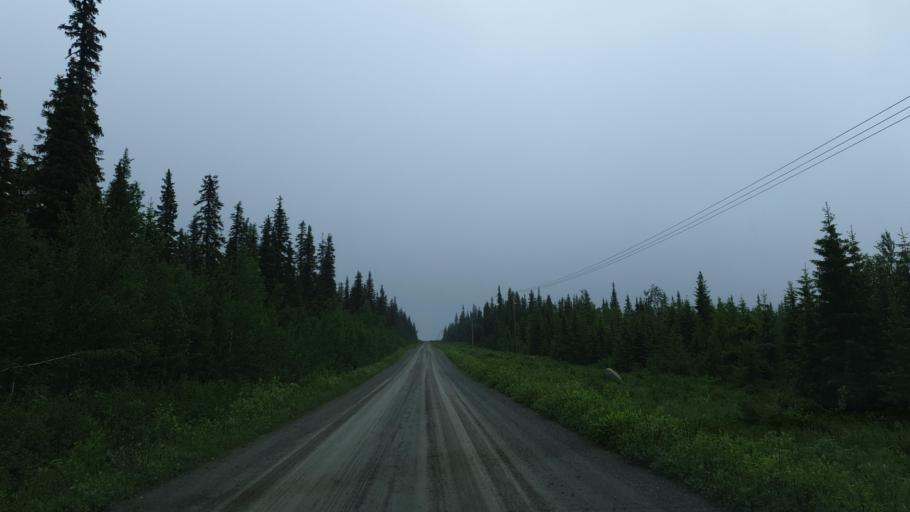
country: SE
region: Vaesterbotten
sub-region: Vilhelmina Kommun
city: Sjoberg
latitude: 65.3201
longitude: 15.9416
